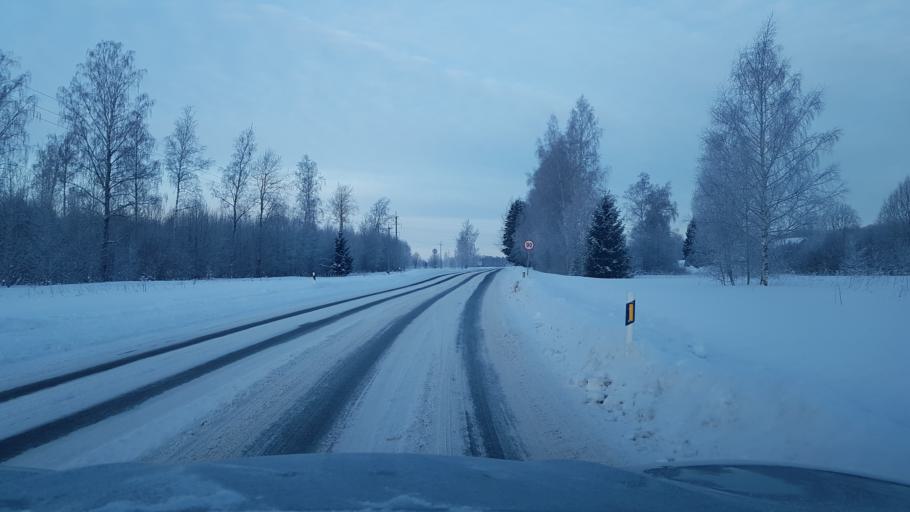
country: EE
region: Ida-Virumaa
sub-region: Johvi vald
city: Johvi
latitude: 59.3389
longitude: 27.4663
